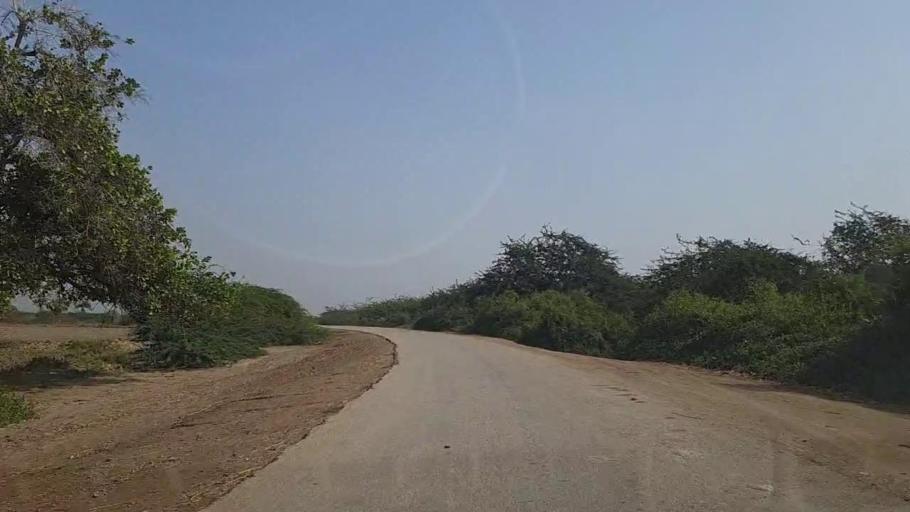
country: PK
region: Sindh
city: Keti Bandar
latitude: 24.2433
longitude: 67.7019
